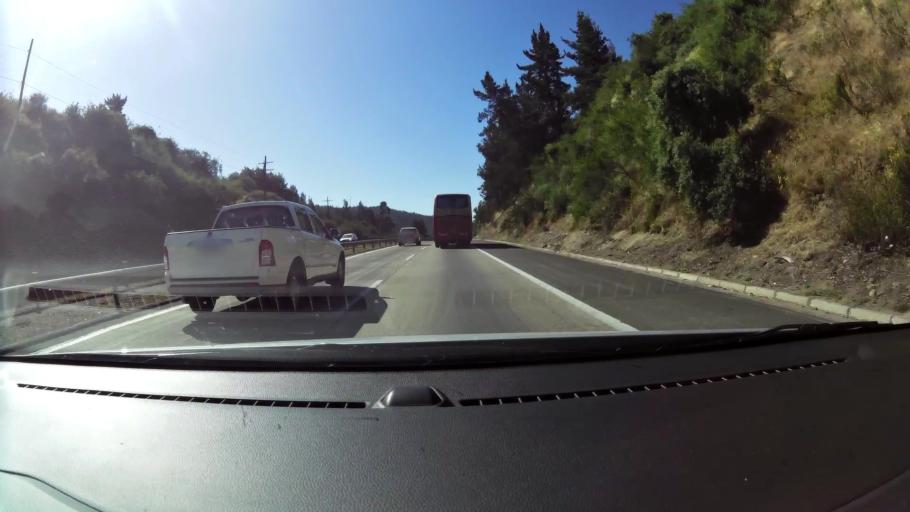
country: CL
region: Valparaiso
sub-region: Provincia de Marga Marga
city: Quilpue
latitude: -33.2332
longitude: -71.4630
